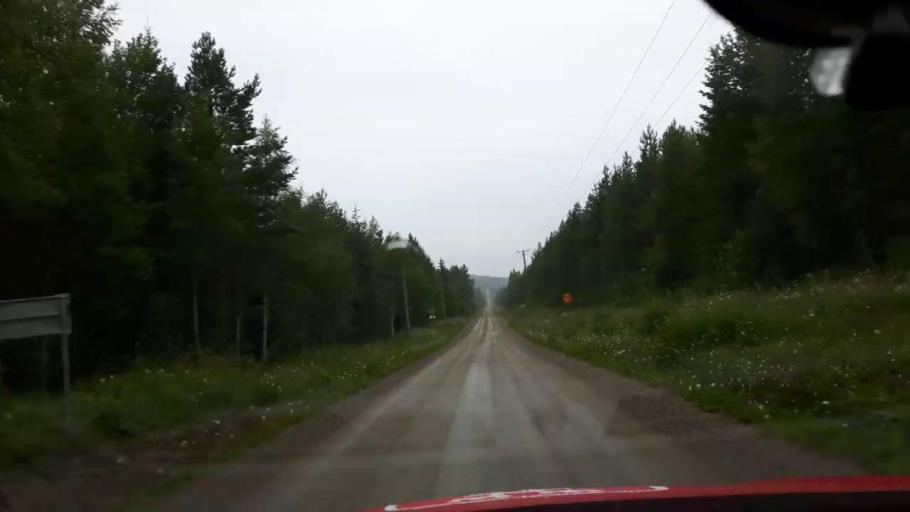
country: SE
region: Jaemtland
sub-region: OEstersunds Kommun
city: Brunflo
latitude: 62.7718
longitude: 14.9966
